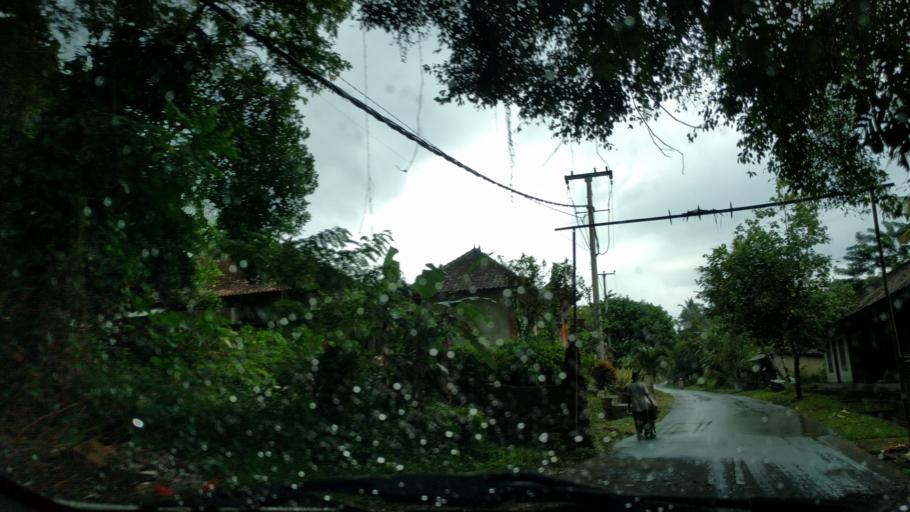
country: ID
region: Bali
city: Bunutan
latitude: -8.4783
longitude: 115.2588
